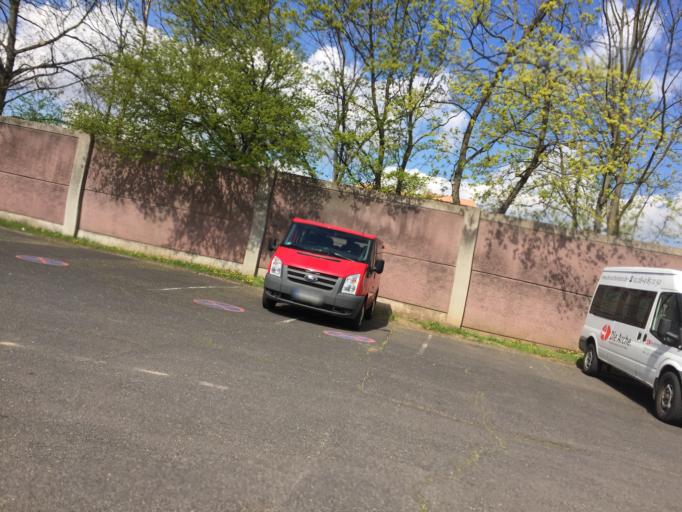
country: DE
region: North Rhine-Westphalia
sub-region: Regierungsbezirk Koln
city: Bonn
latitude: 50.7484
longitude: 7.0784
